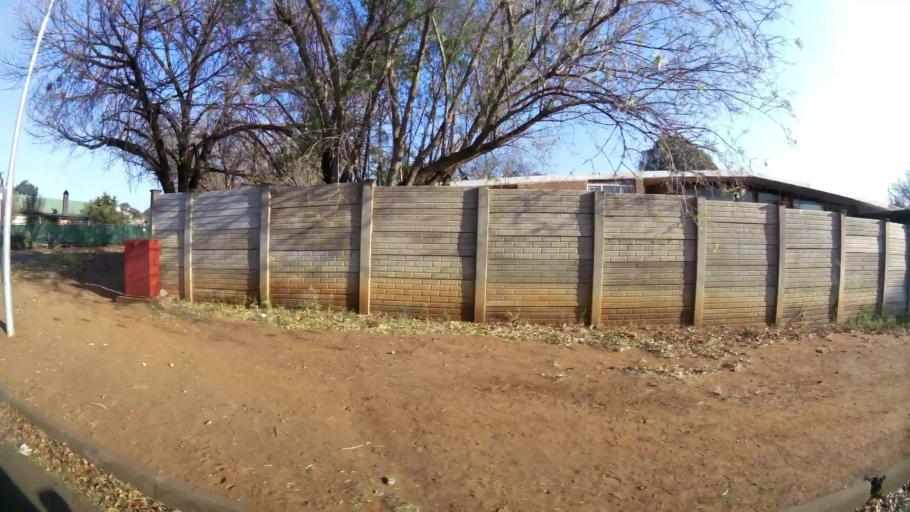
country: ZA
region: Orange Free State
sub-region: Mangaung Metropolitan Municipality
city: Bloemfontein
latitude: -29.1506
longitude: 26.2007
